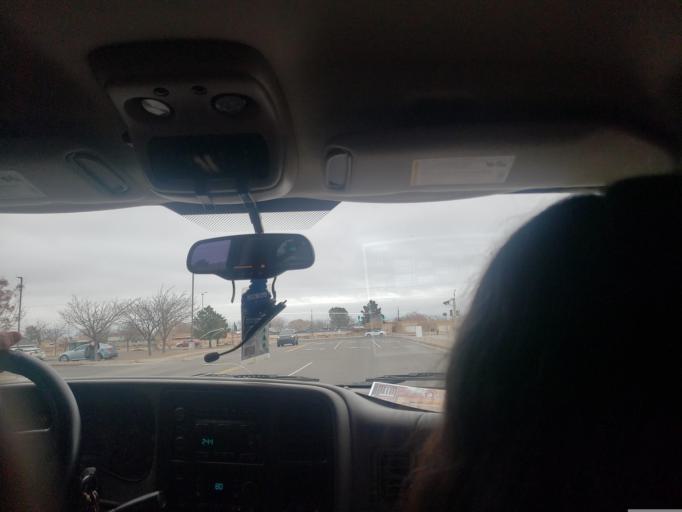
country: US
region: New Mexico
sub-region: Bernalillo County
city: Albuquerque
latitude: 35.0912
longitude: -106.7119
